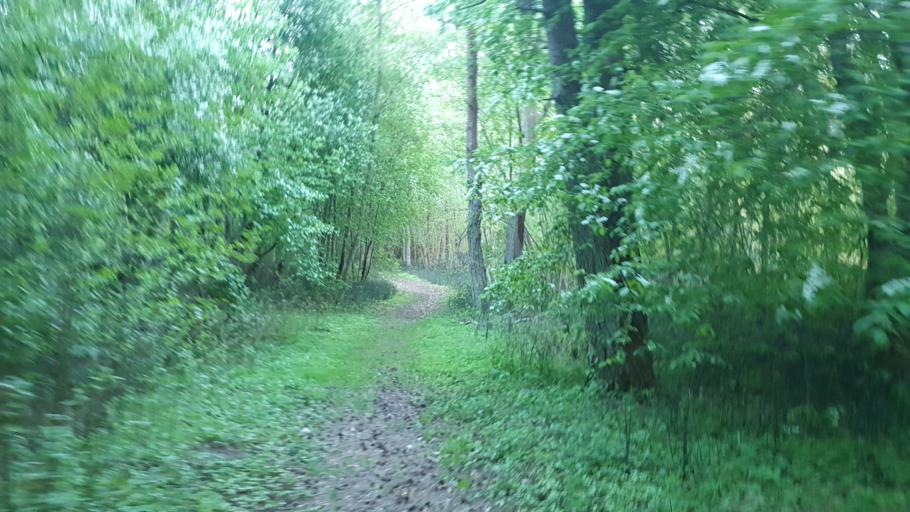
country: LV
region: Ikskile
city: Ikskile
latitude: 56.8338
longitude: 24.4405
